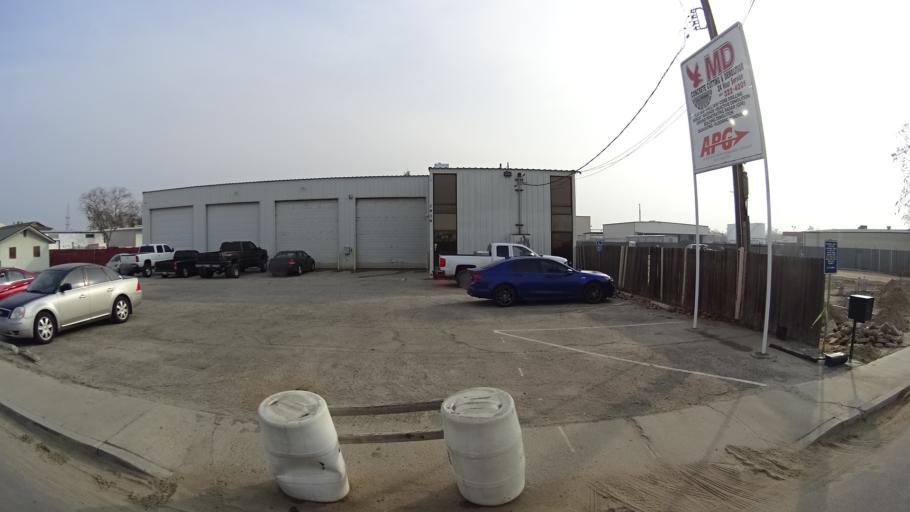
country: US
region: California
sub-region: Kern County
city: Bakersfield
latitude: 35.3873
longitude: -119.0521
